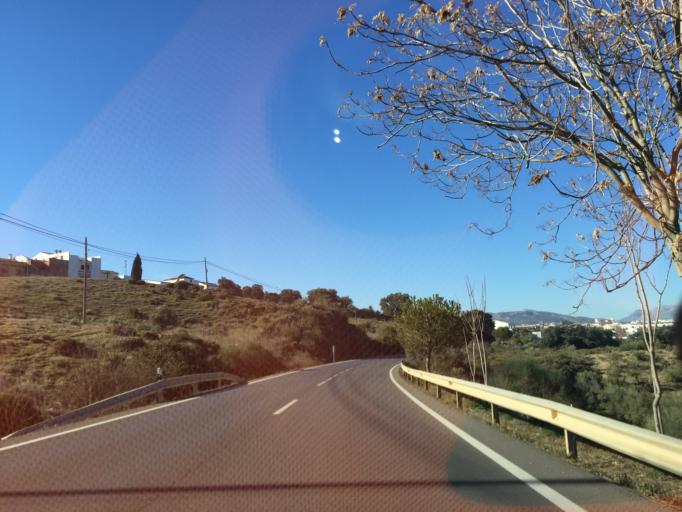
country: ES
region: Andalusia
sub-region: Provincia de Malaga
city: Ronda
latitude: 36.7588
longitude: -5.1412
